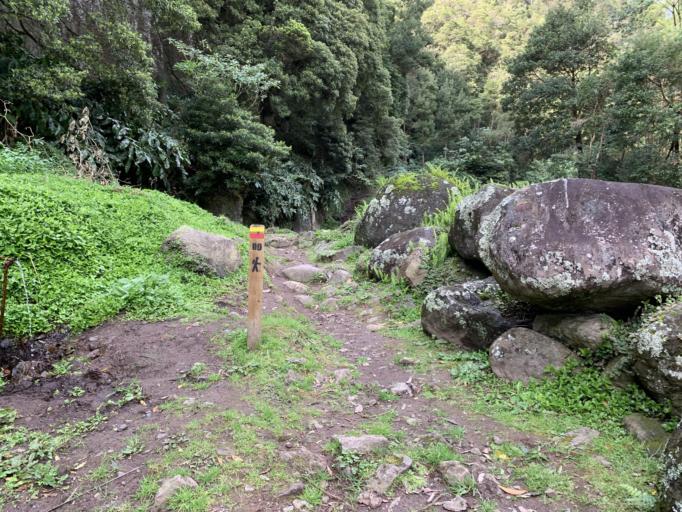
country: PT
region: Azores
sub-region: Povoacao
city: Furnas
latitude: 37.7517
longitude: -25.2023
